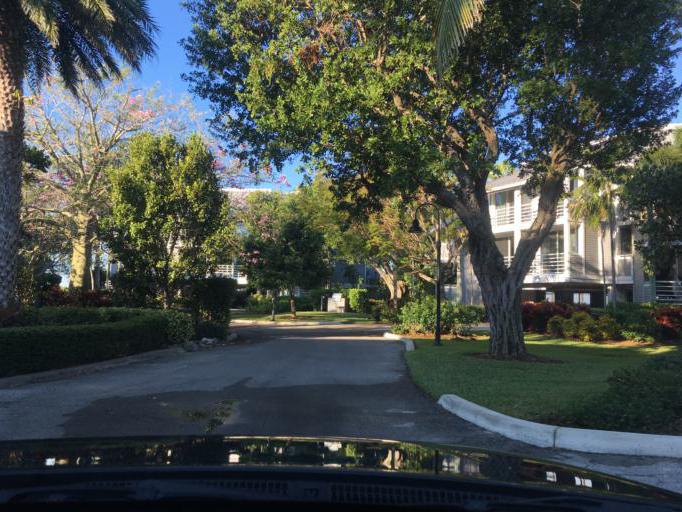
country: US
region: Florida
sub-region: Lee County
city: Pine Island Center
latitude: 26.5518
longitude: -82.1997
